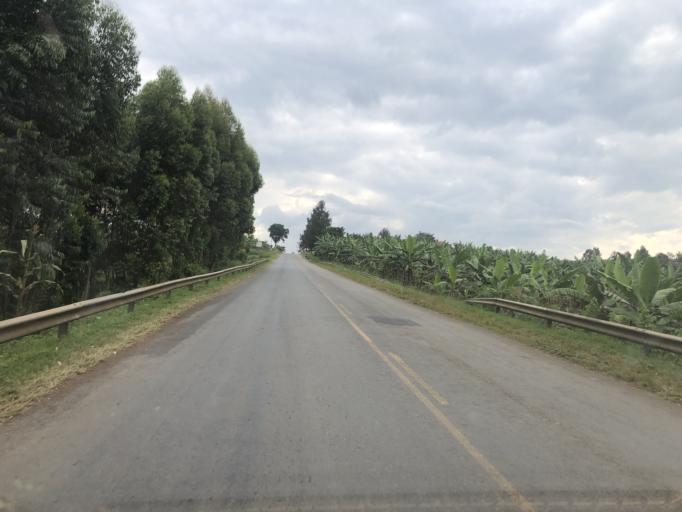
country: UG
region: Western Region
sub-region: Sheema District
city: Kibingo
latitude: -0.5790
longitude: 30.4111
